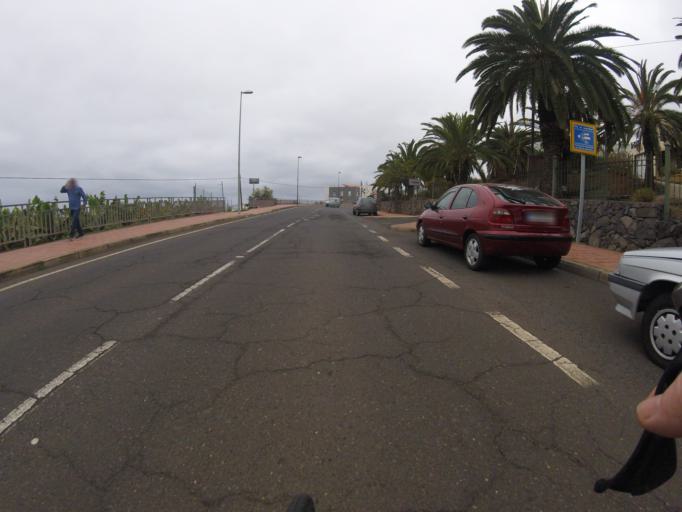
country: ES
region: Canary Islands
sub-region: Provincia de Santa Cruz de Tenerife
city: Tegueste
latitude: 28.5319
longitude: -16.3705
